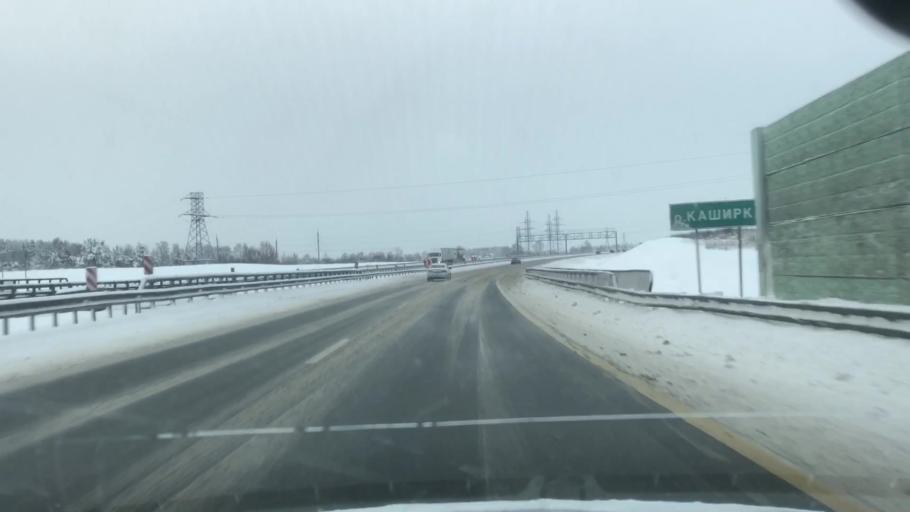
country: RU
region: Moskovskaya
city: Mikhnevo
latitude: 55.1256
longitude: 37.9340
